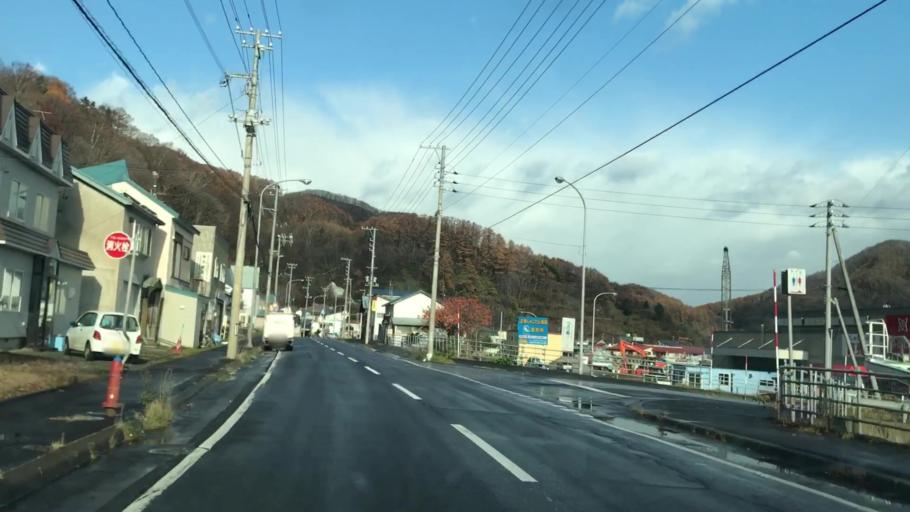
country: JP
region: Hokkaido
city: Yoichi
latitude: 43.2710
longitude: 140.6369
